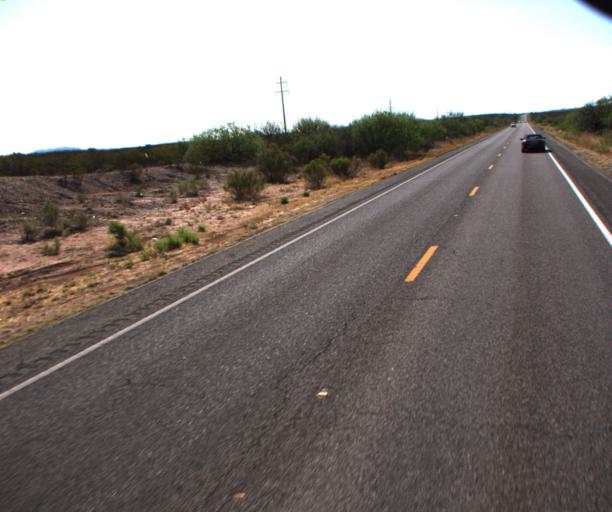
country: US
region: Arizona
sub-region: Cochise County
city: Tombstone
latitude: 31.7593
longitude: -110.1102
